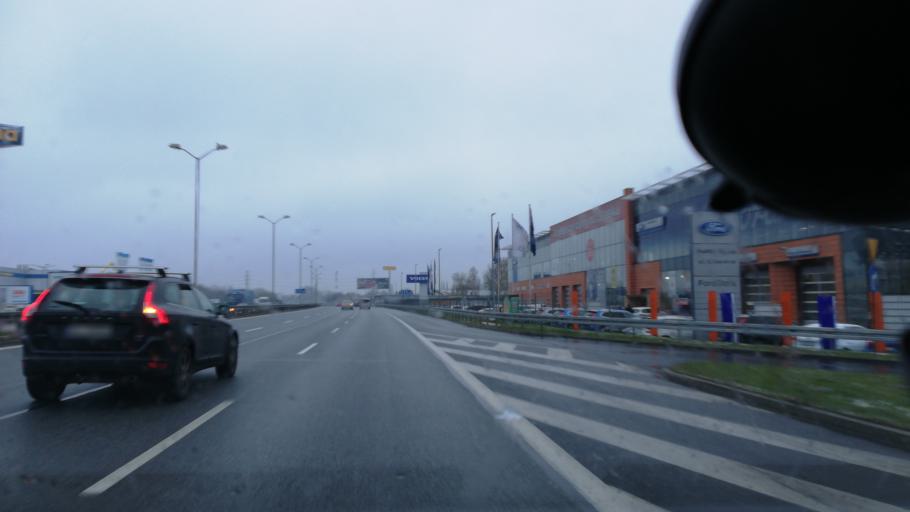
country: PL
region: Silesian Voivodeship
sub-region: Chorzow
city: Chorzow
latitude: 50.2792
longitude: 18.9539
